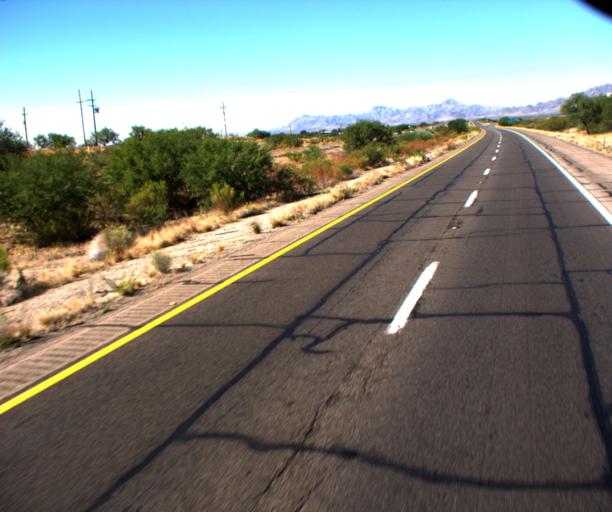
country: US
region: Arizona
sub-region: Pima County
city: Arivaca Junction
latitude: 31.7337
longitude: -111.0545
